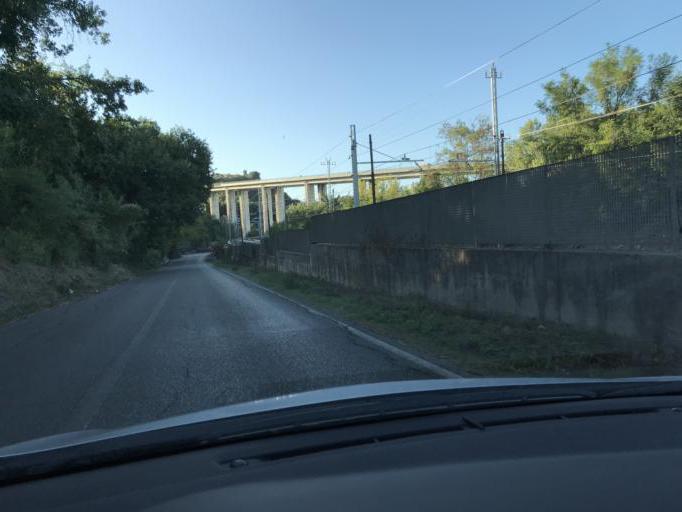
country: IT
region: Latium
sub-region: Provincia di Viterbo
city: Orte
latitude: 42.4487
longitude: 12.3909
